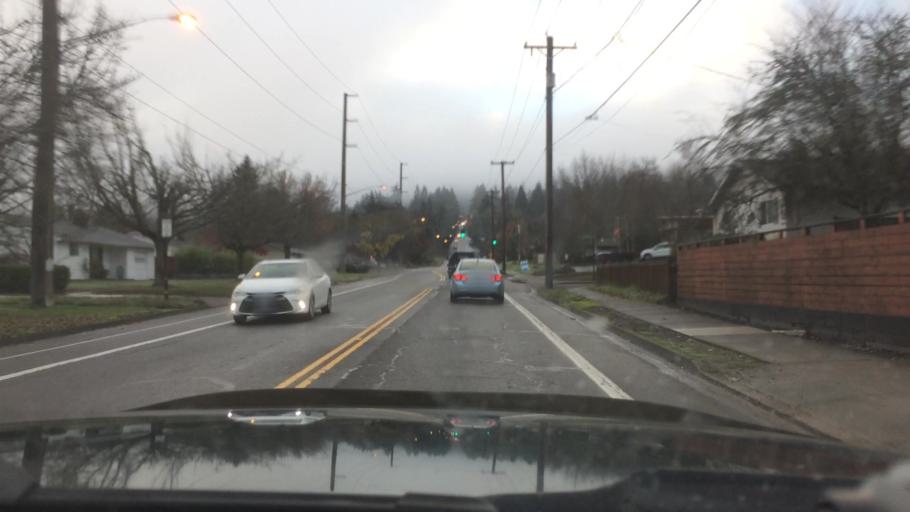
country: US
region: Oregon
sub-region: Lane County
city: Eugene
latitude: 44.0345
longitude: -123.1179
